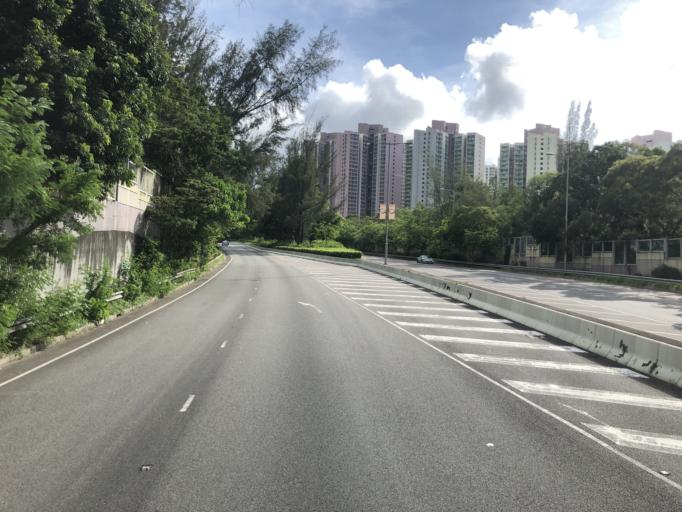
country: HK
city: Tai O
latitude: 22.2884
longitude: 113.9464
